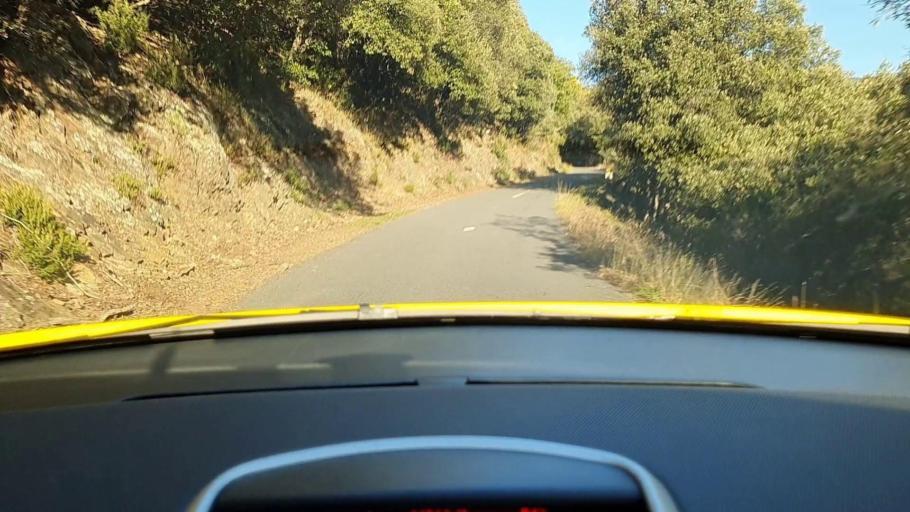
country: FR
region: Languedoc-Roussillon
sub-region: Departement du Gard
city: Sumene
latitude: 44.0228
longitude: 3.7522
